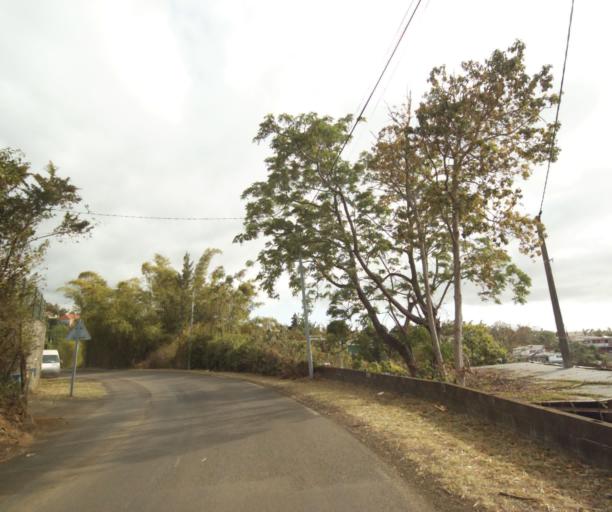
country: RE
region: Reunion
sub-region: Reunion
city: Saint-Paul
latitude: -21.0366
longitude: 55.3074
